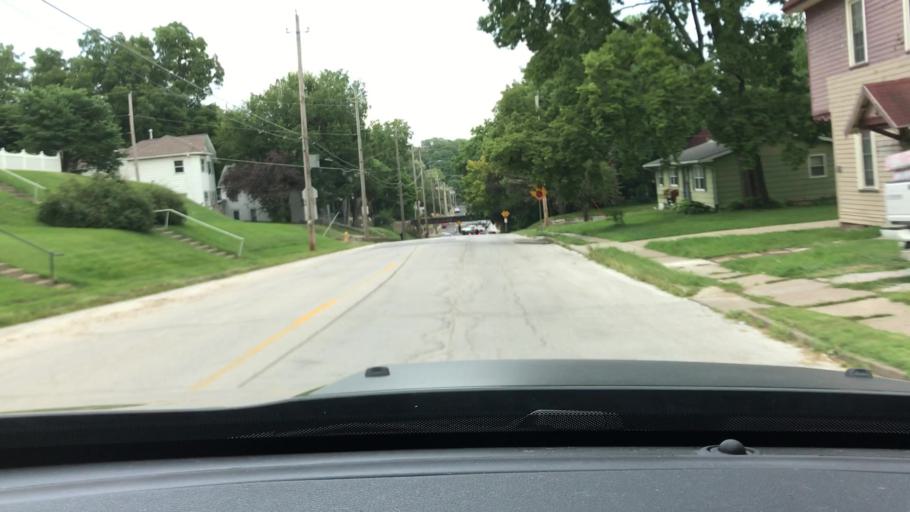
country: US
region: Iowa
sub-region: Scott County
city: Davenport
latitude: 41.5322
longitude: -90.5486
